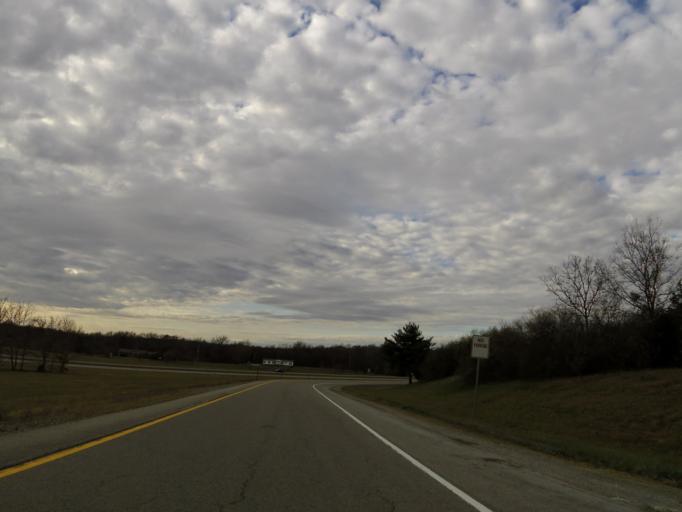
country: US
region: Illinois
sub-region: Jefferson County
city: Mount Vernon
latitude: 38.3635
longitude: -89.0367
